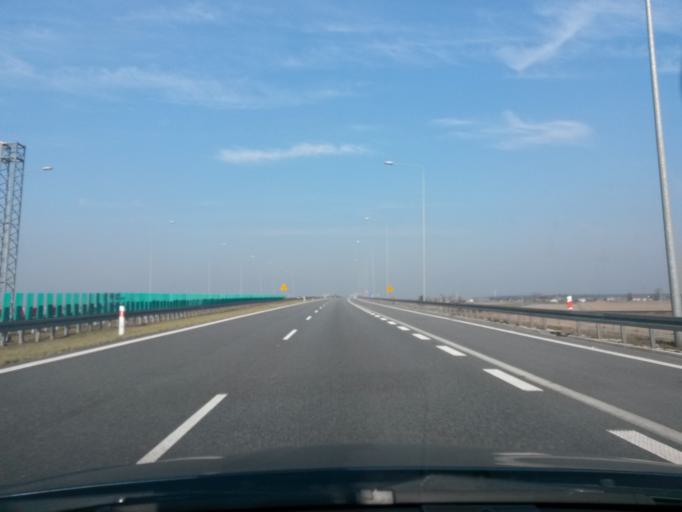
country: PL
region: Lodz Voivodeship
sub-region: Powiat kutnowski
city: Krzyzanow
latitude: 52.2271
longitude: 19.4625
